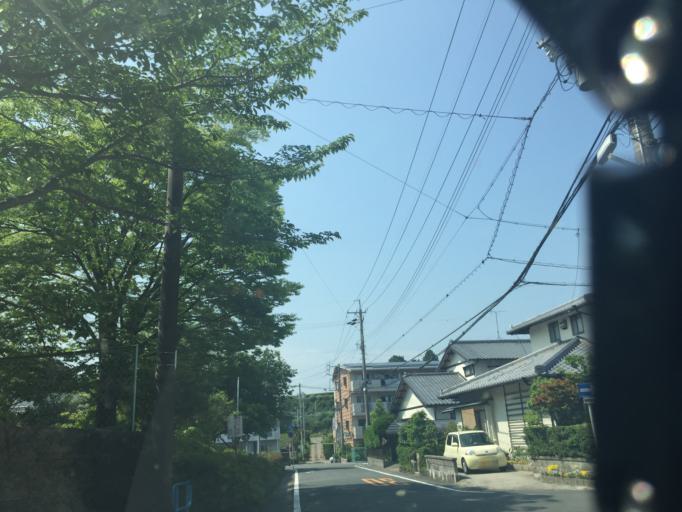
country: JP
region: Shizuoka
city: Kakegawa
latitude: 34.7632
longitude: 138.0036
